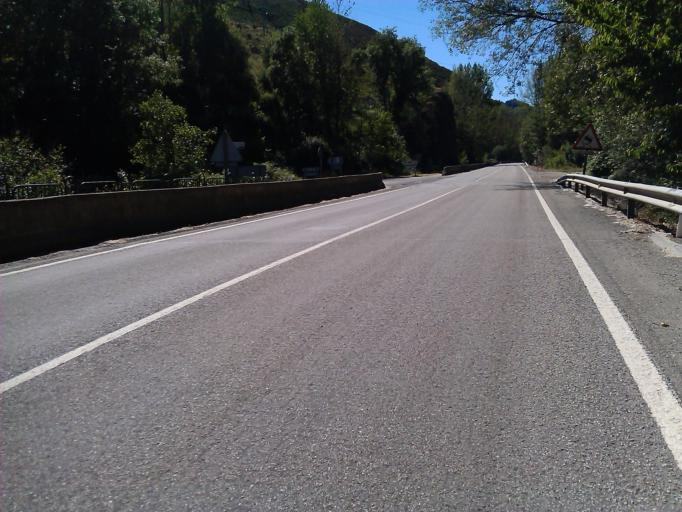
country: ES
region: Castille and Leon
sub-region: Provincia de Leon
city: Trabadelo
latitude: 42.6548
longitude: -6.9014
